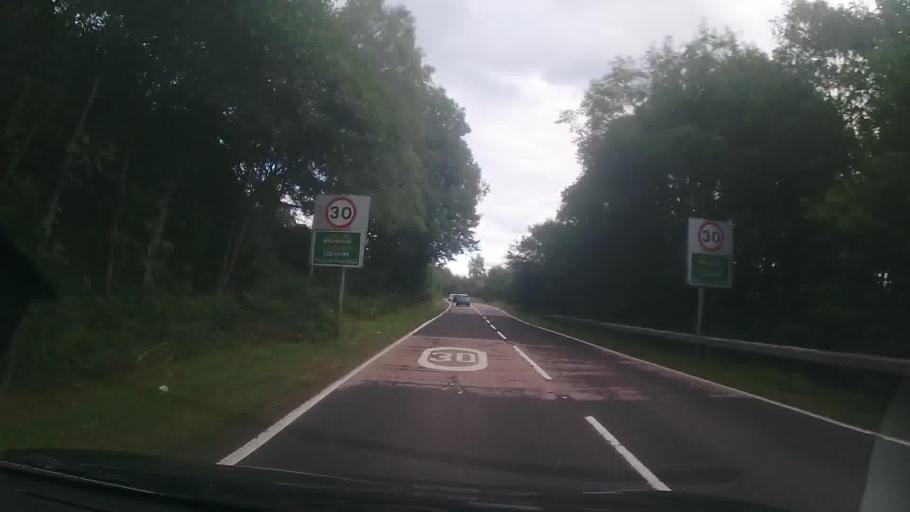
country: GB
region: Scotland
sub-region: Argyll and Bute
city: Garelochhead
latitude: 56.3926
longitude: -5.0617
